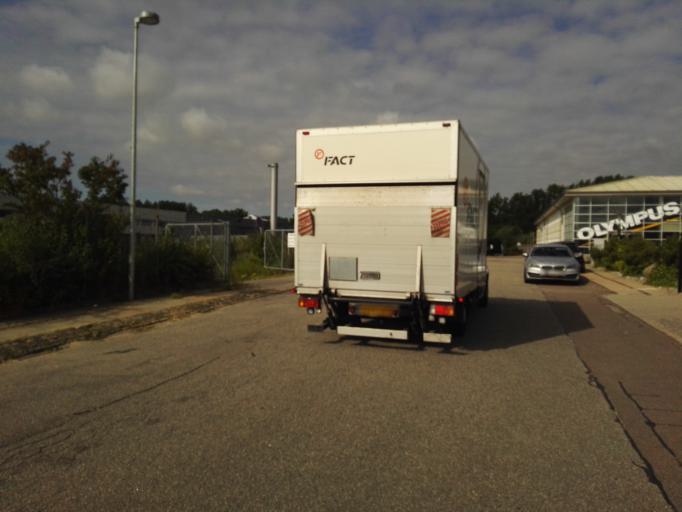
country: DK
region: Capital Region
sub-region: Ballerup Kommune
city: Ballerup
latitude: 55.7239
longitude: 12.3722
